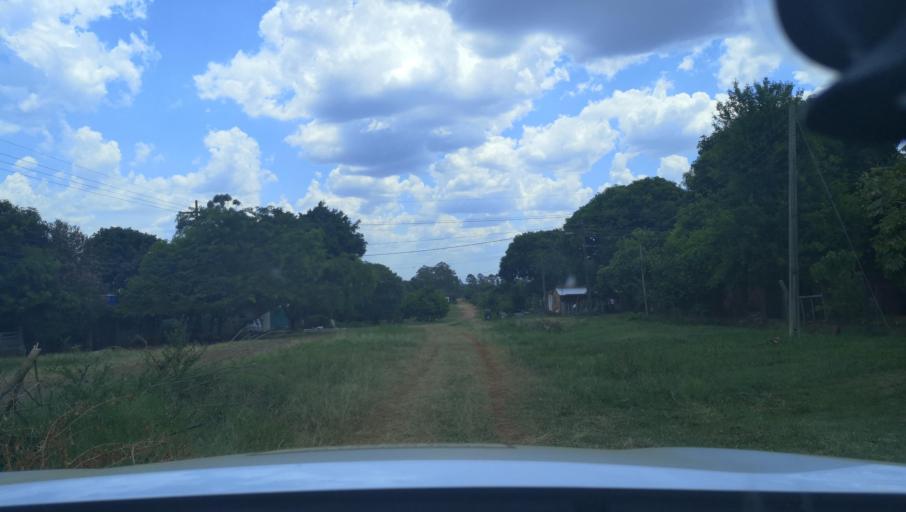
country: PY
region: Itapua
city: Carmen del Parana
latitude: -27.1716
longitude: -56.2338
